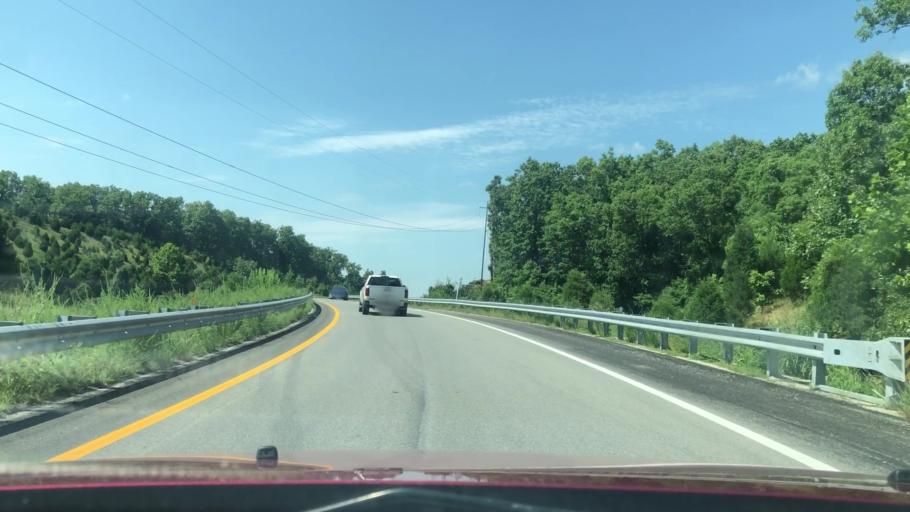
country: US
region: Missouri
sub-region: Taney County
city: Branson
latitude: 36.6766
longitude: -93.3155
